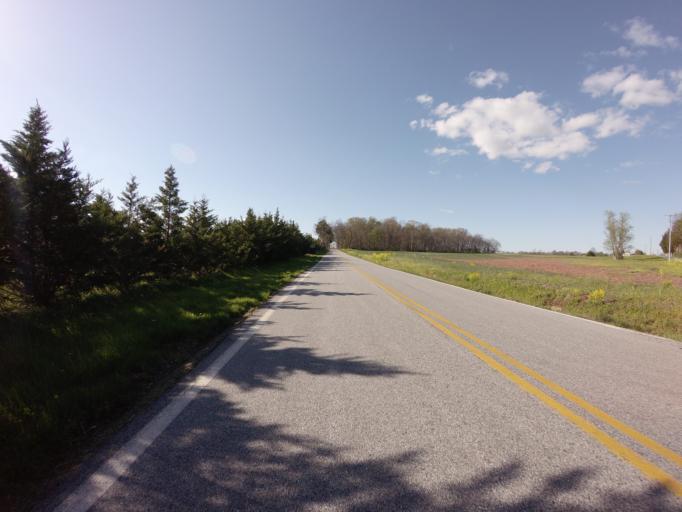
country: US
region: Maryland
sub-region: Frederick County
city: Emmitsburg
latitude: 39.6338
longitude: -77.2861
